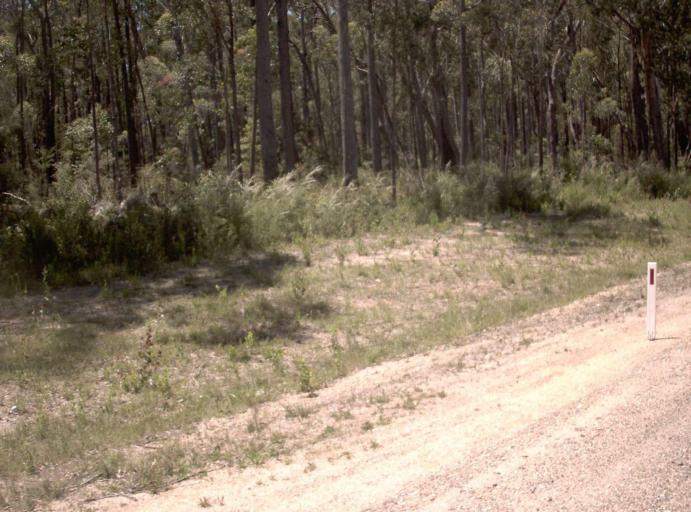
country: AU
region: Victoria
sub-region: East Gippsland
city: Lakes Entrance
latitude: -37.6795
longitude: 148.7744
